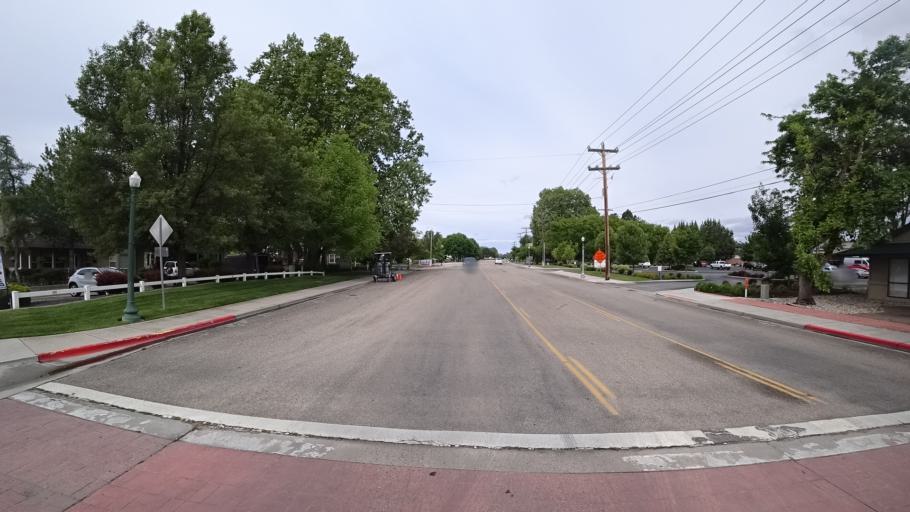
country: US
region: Idaho
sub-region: Ada County
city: Eagle
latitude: 43.6951
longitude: -116.3569
